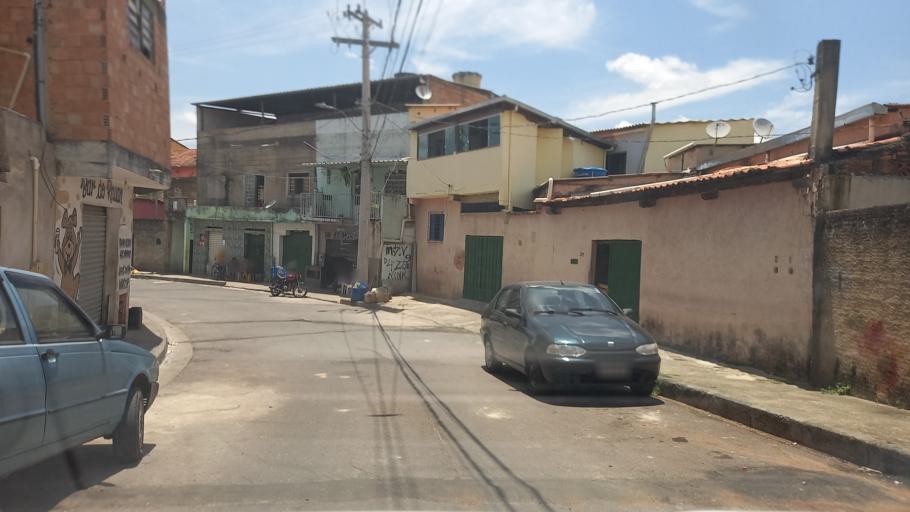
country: BR
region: Minas Gerais
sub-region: Contagem
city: Contagem
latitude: -19.9115
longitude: -44.0083
